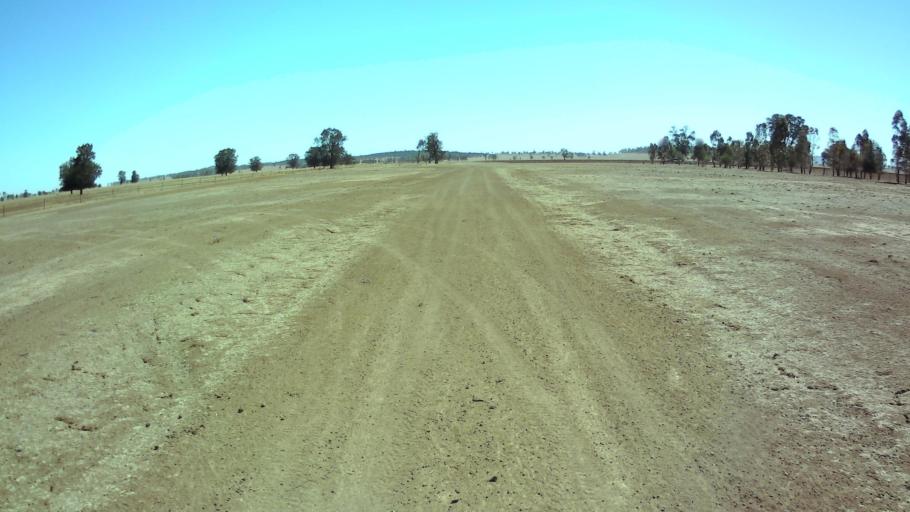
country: AU
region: New South Wales
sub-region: Forbes
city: Forbes
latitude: -33.7144
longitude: 147.6669
